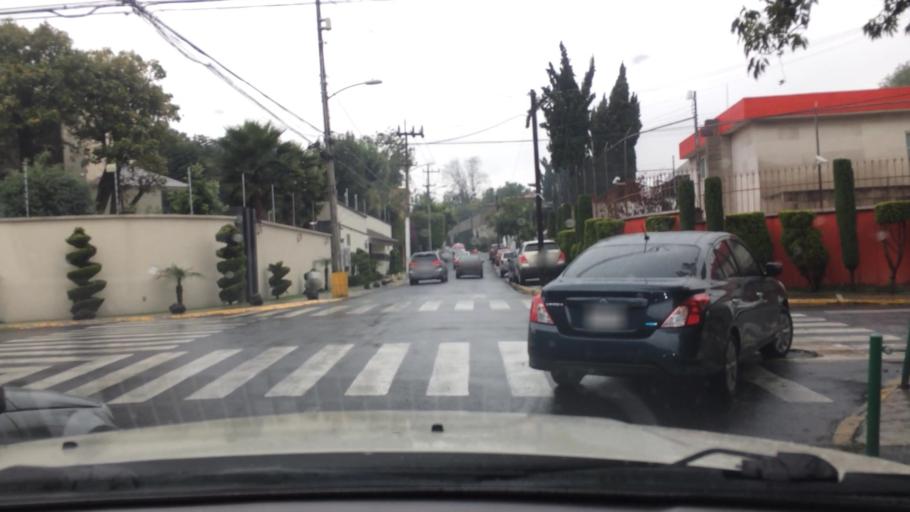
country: MX
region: Mexico City
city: Magdalena Contreras
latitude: 19.3225
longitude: -99.2062
